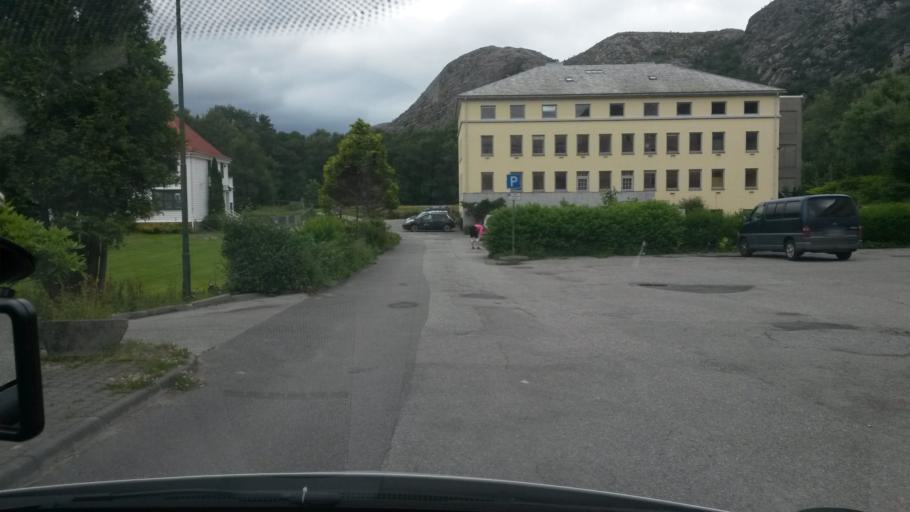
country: NO
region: Rogaland
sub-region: Sandnes
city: Sandnes
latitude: 58.9007
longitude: 5.7802
